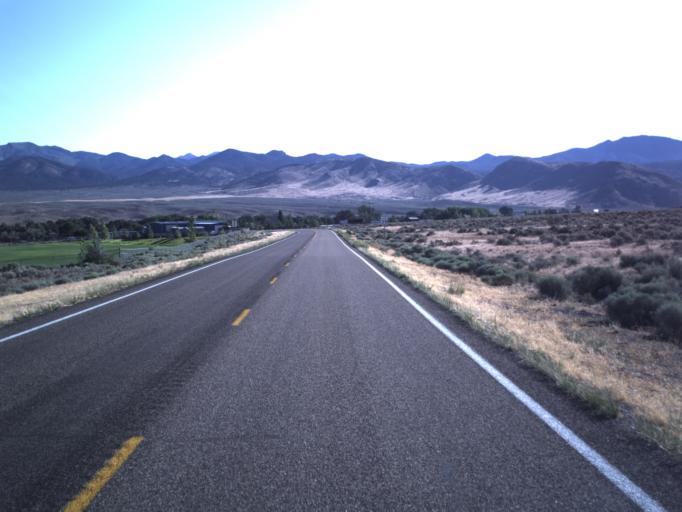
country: US
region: Utah
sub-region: Beaver County
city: Milford
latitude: 38.2060
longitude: -112.9265
